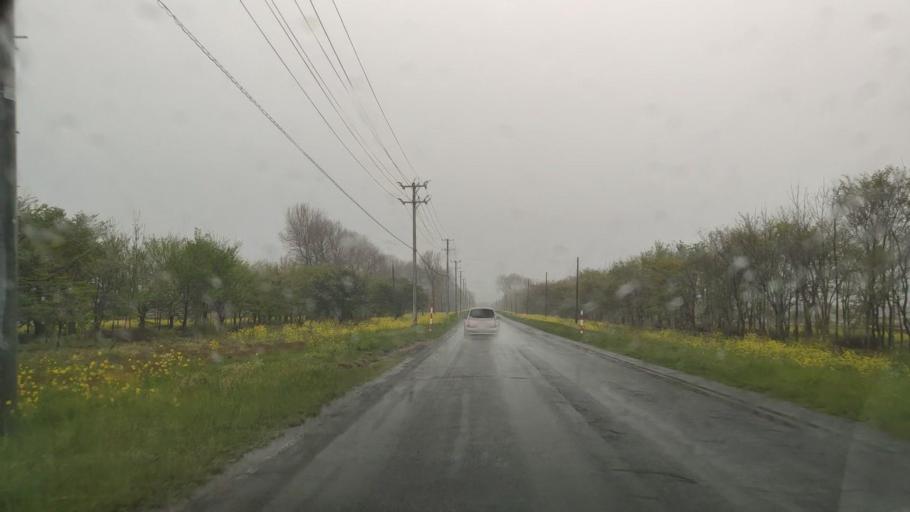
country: JP
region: Akita
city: Tenno
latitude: 39.9574
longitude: 139.9459
